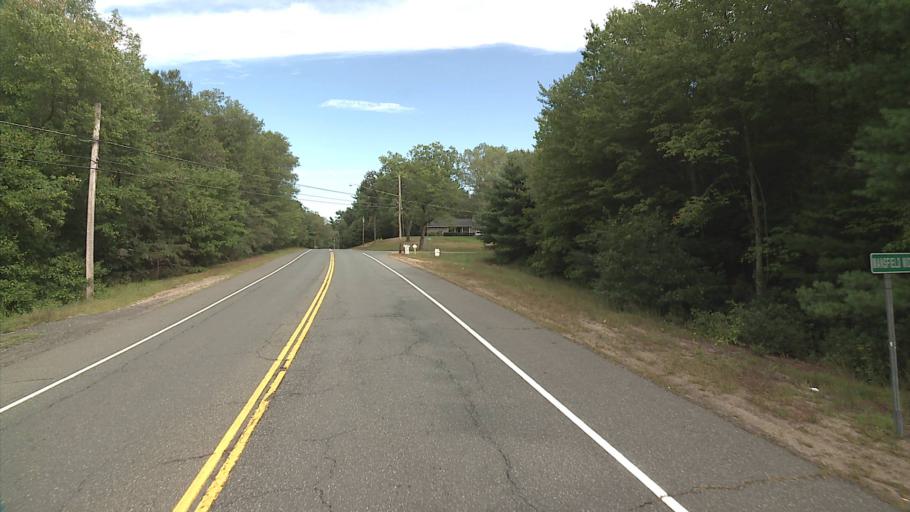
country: US
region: Connecticut
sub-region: Tolland County
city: Mansfield City
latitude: 41.7498
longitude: -72.2602
